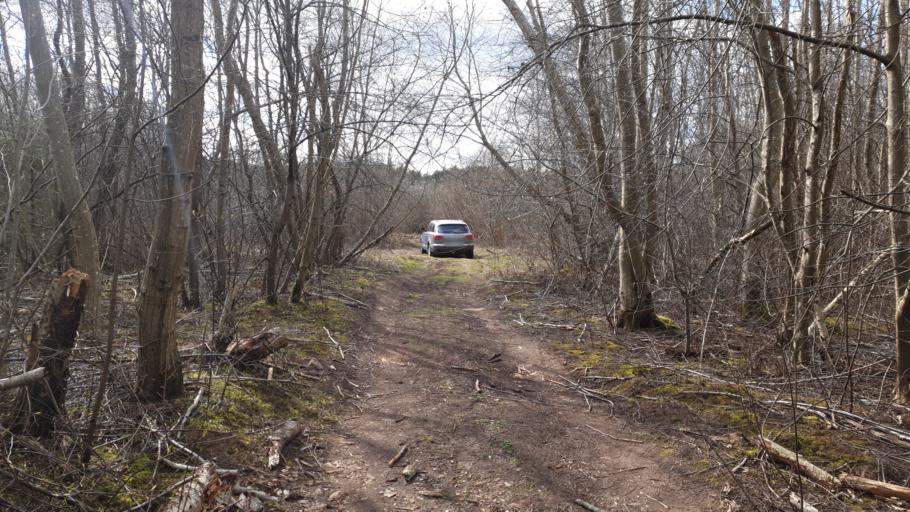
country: LT
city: Grigiskes
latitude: 54.7243
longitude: 25.0278
